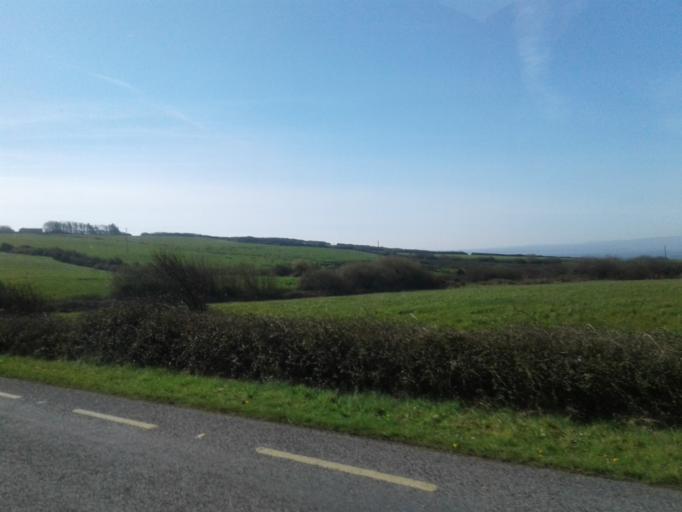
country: IE
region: Munster
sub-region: An Clar
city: Kilrush
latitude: 52.6226
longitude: -9.4652
